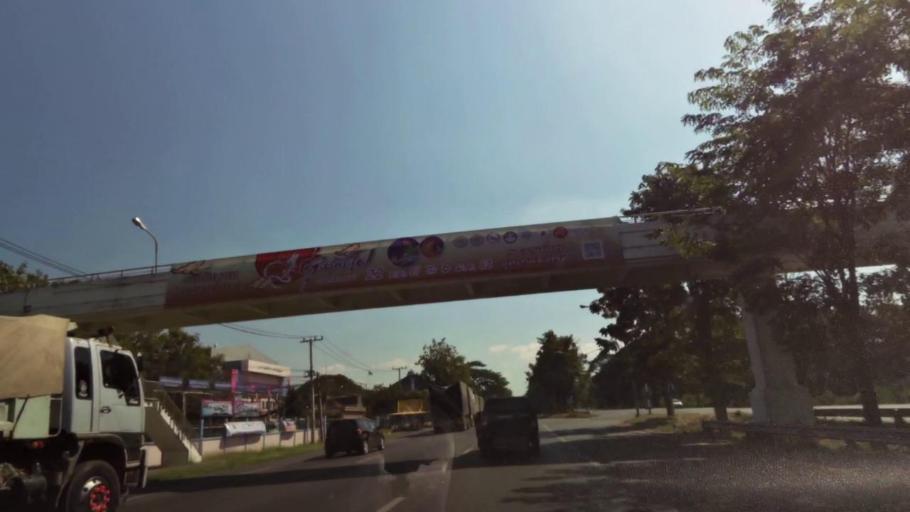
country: TH
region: Nakhon Sawan
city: Nakhon Sawan
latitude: 15.6647
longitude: 100.1291
